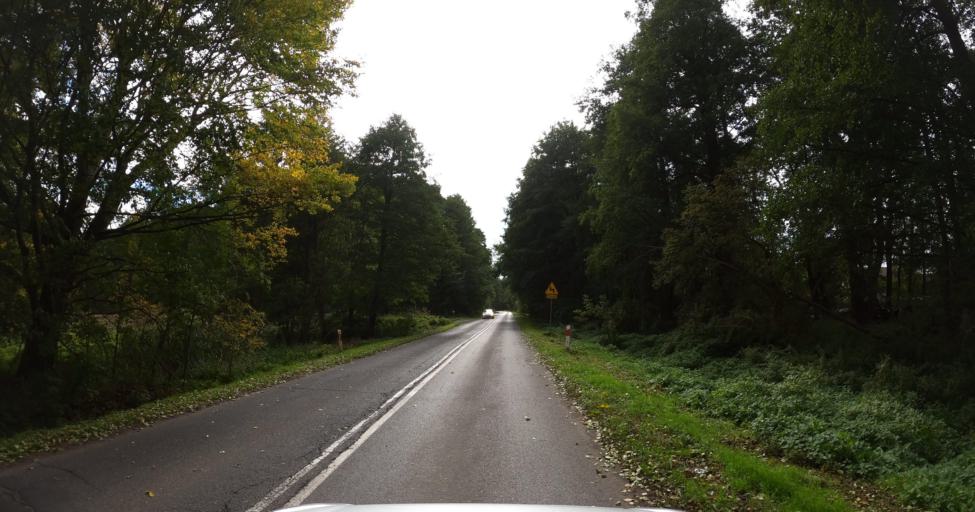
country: PL
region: Lubusz
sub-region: Zielona Gora
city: Zielona Gora
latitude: 51.9936
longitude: 15.5663
